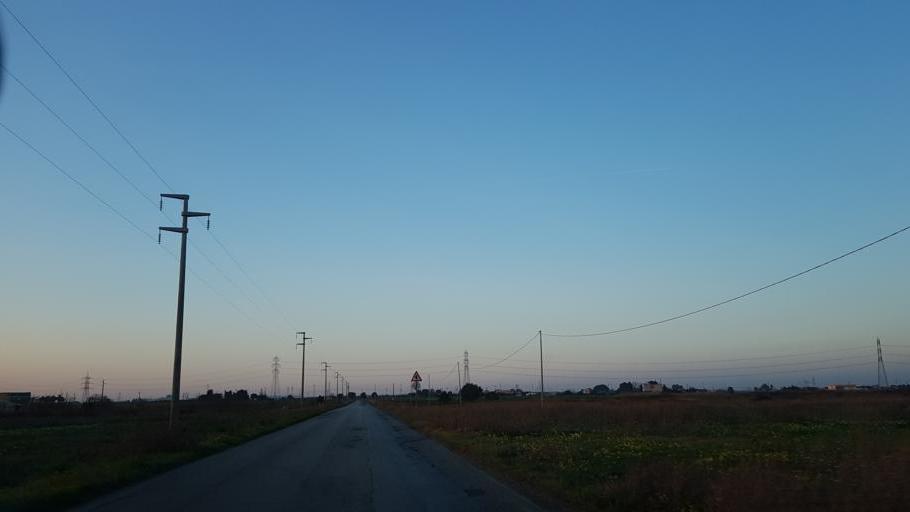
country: IT
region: Apulia
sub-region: Provincia di Brindisi
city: La Rosa
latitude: 40.5850
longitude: 17.9468
